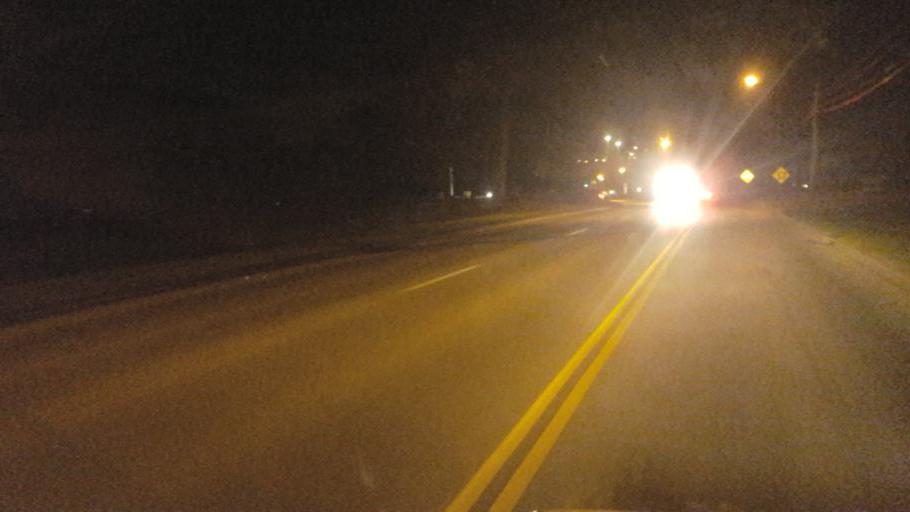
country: US
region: Ohio
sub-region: Wayne County
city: Wooster
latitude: 40.7854
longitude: -81.9328
